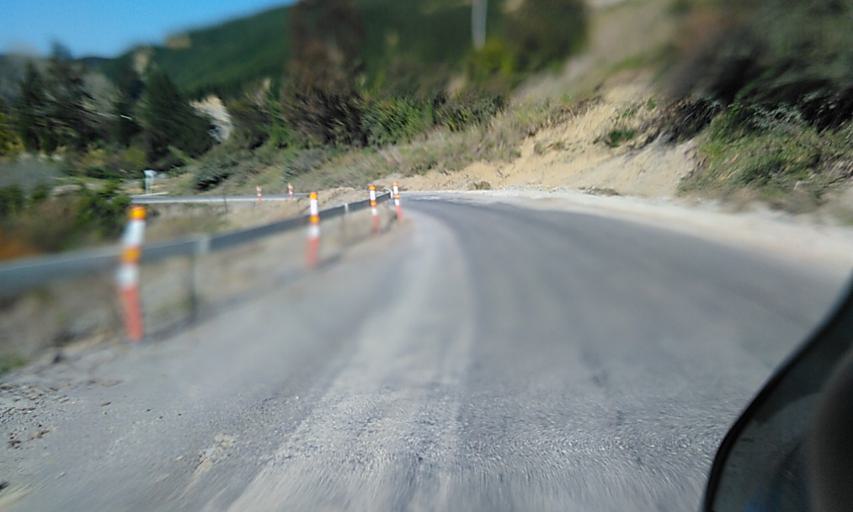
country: NZ
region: Gisborne
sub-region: Gisborne District
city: Gisborne
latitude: -38.3249
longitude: 178.1584
